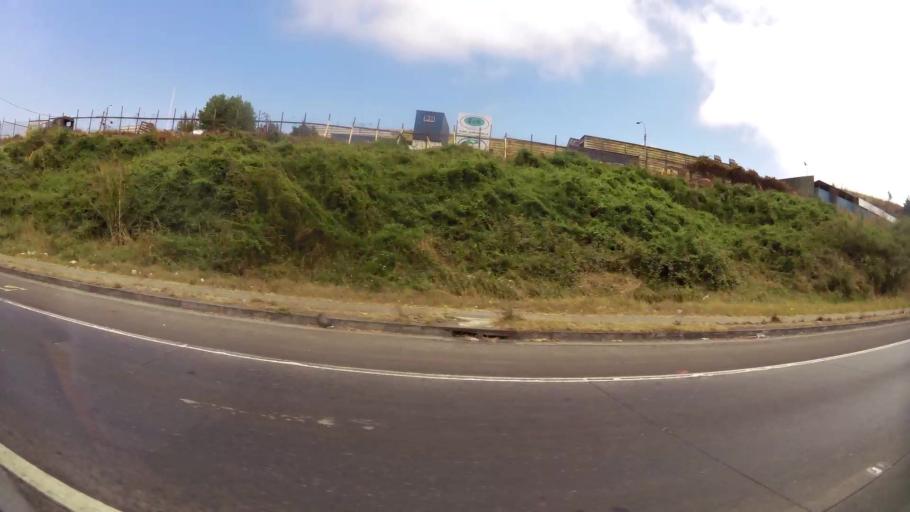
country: CL
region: Biobio
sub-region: Provincia de Concepcion
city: Concepcion
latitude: -36.8003
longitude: -73.0435
